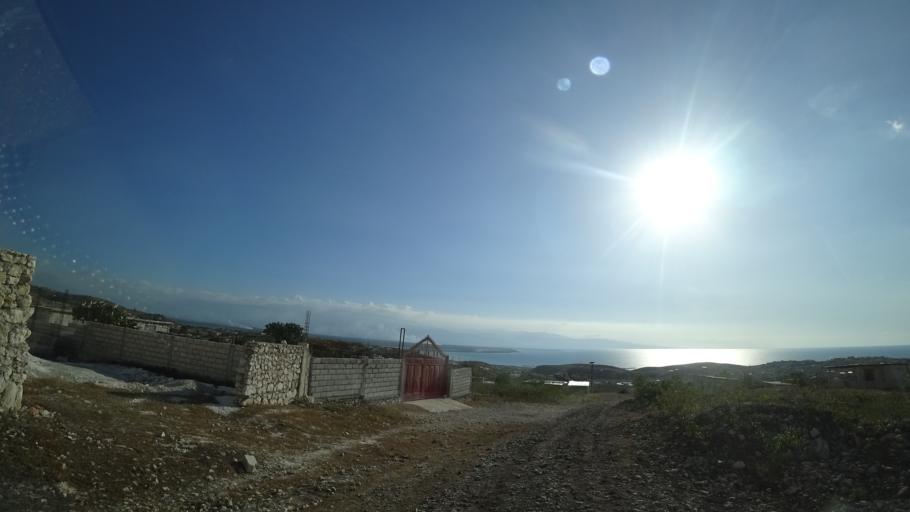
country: HT
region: Ouest
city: Cabaret
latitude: 18.6897
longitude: -72.3109
